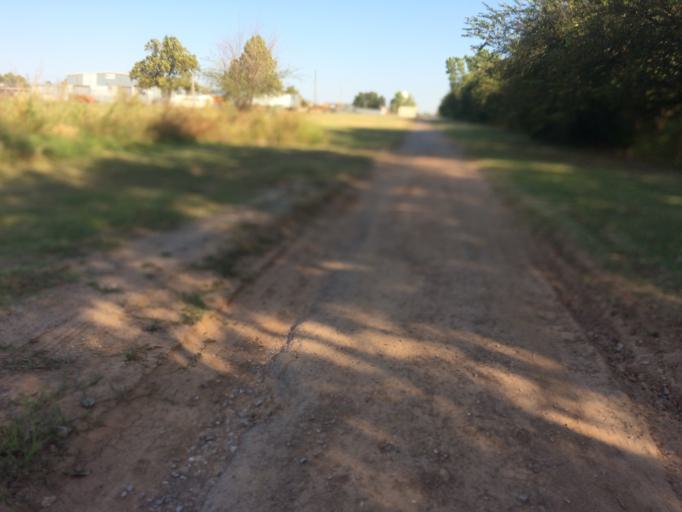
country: US
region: Oklahoma
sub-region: Cleveland County
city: Norman
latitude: 35.1839
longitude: -97.4322
